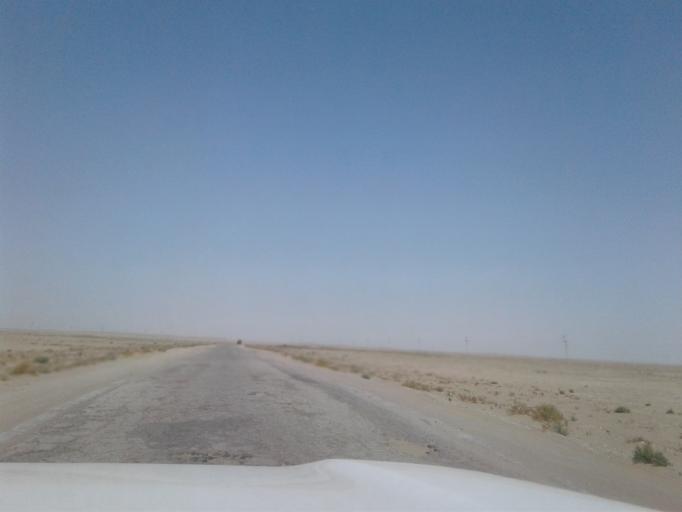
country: TM
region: Balkan
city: Gumdag
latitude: 38.3398
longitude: 54.3603
